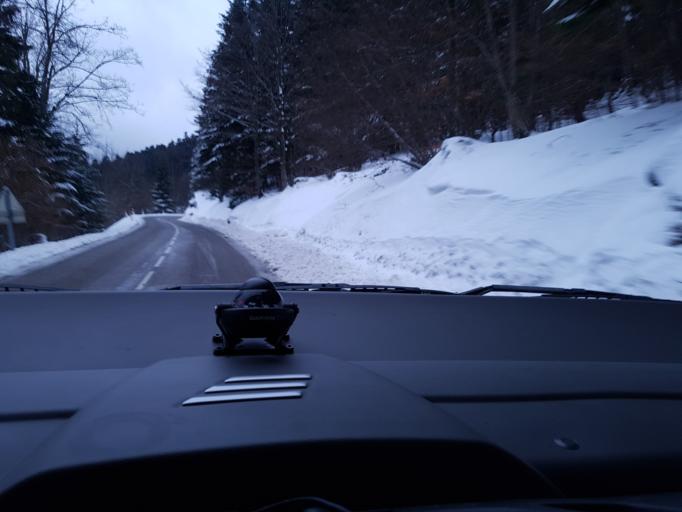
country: FR
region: Alsace
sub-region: Departement du Haut-Rhin
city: Lapoutroie
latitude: 48.2024
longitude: 7.1283
